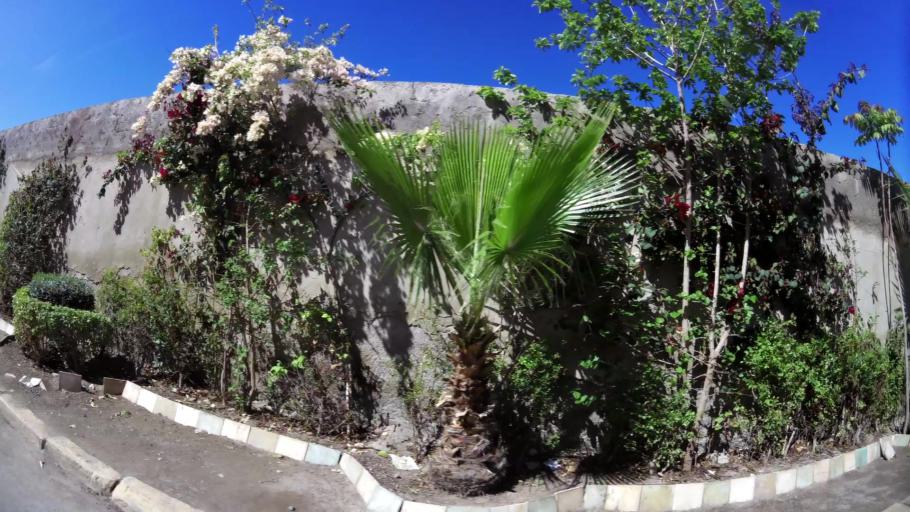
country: MA
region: Marrakech-Tensift-Al Haouz
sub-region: Marrakech
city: Marrakesh
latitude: 31.6360
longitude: -8.0031
